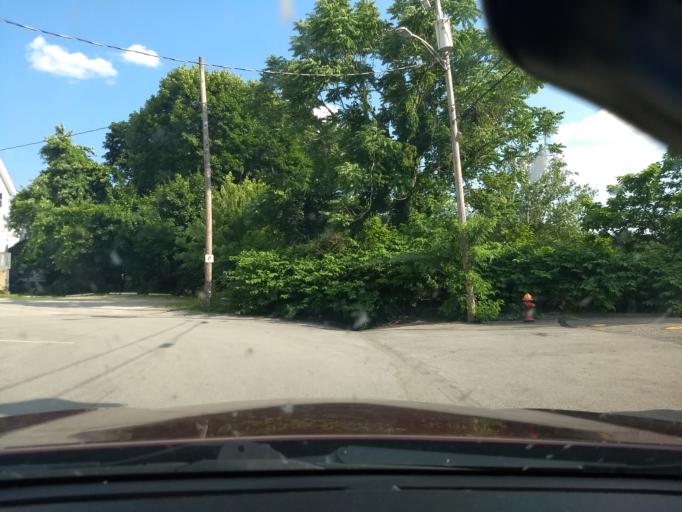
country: US
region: Pennsylvania
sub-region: Westmoreland County
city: Irwin
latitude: 40.3297
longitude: -79.7116
